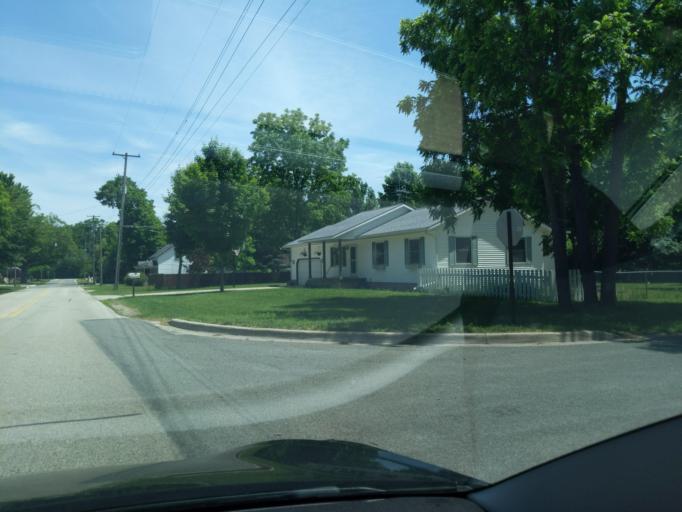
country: US
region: Michigan
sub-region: Muskegon County
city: Montague
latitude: 43.4150
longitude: -86.3638
